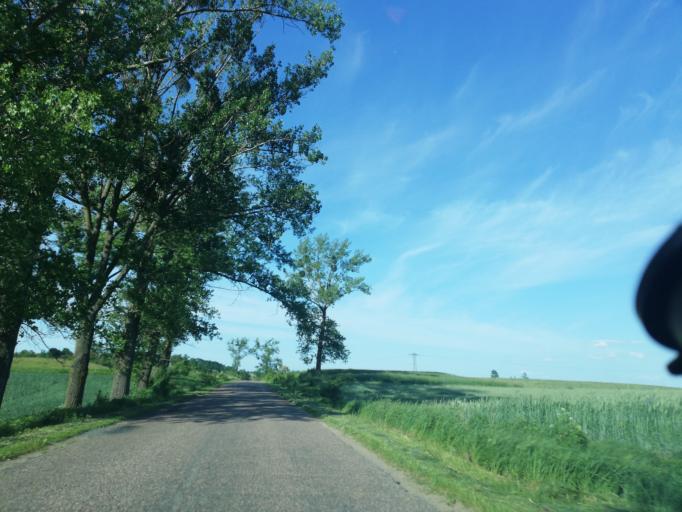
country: PL
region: Kujawsko-Pomorskie
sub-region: Powiat golubsko-dobrzynski
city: Golub-Dobrzyn
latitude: 53.0330
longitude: 19.0751
